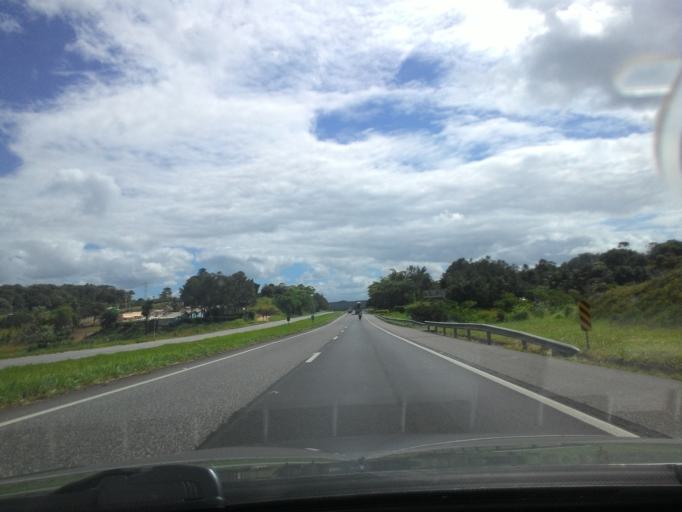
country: BR
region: Sao Paulo
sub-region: Pariquera-Acu
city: Pariquera Acu
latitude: -24.6365
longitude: -47.9106
